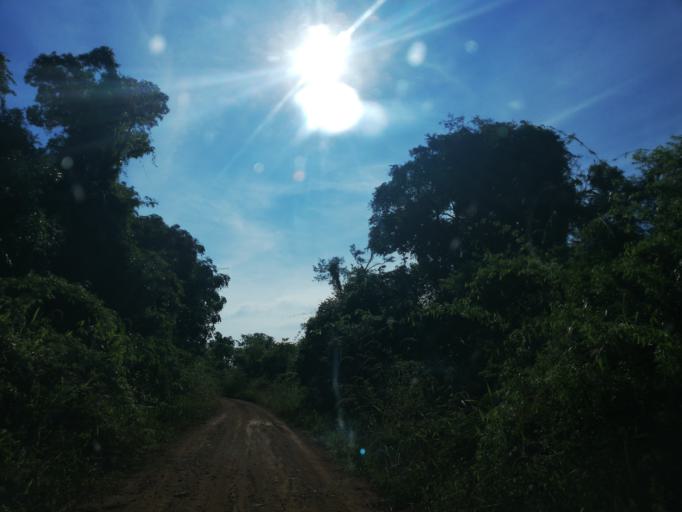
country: AR
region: Misiones
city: Dos de Mayo
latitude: -27.0144
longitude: -54.4302
